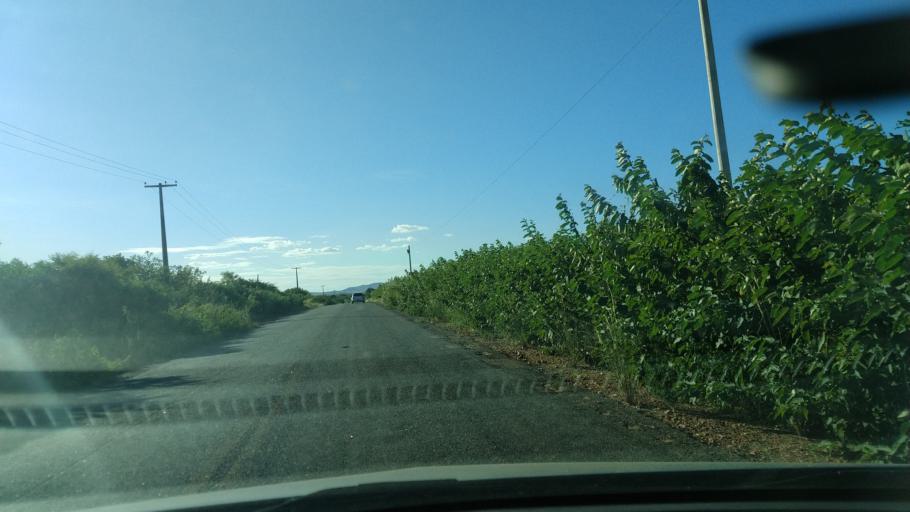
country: BR
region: Rio Grande do Norte
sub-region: Sao Jose Do Campestre
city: Sao Jose do Campestre
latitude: -6.4072
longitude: -35.6532
